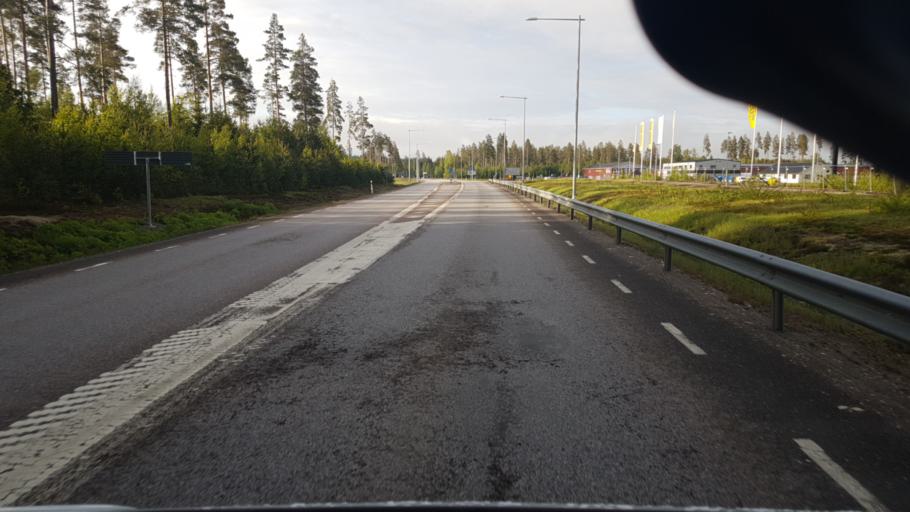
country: SE
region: Vaermland
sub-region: Eda Kommun
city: Charlottenberg
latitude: 59.8744
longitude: 12.2882
